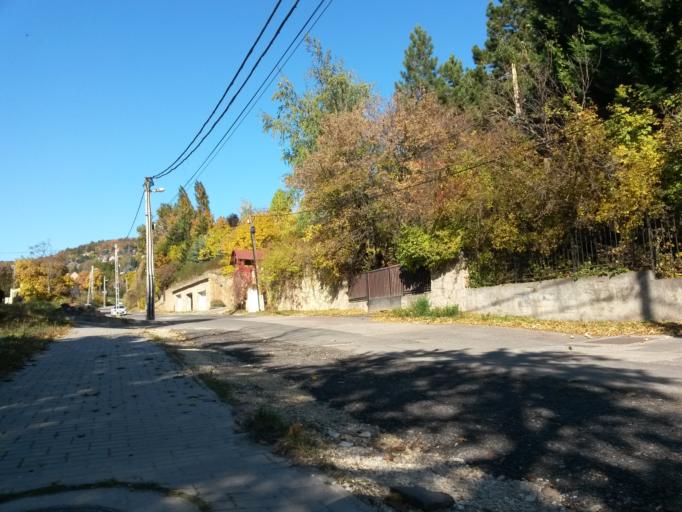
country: HU
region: Pest
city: Budaors
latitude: 47.4797
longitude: 18.9822
